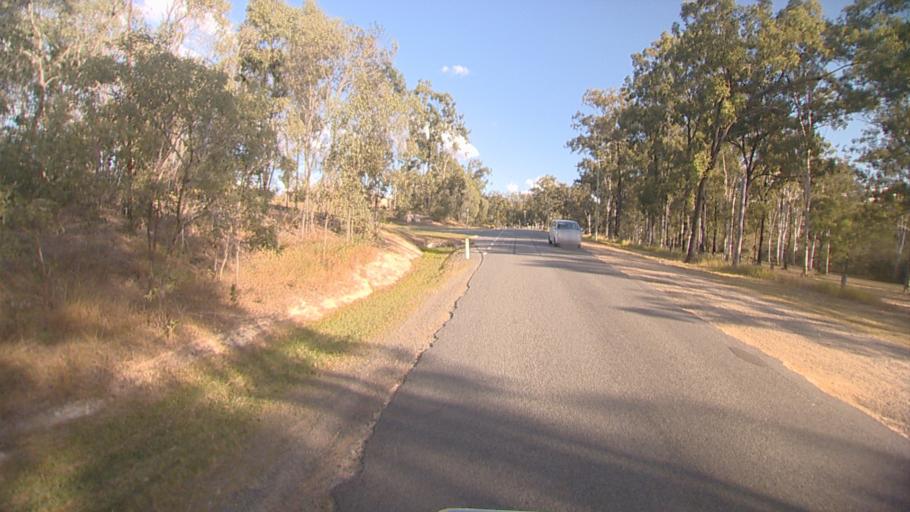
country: AU
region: Queensland
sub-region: Logan
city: North Maclean
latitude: -27.7449
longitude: 152.9413
